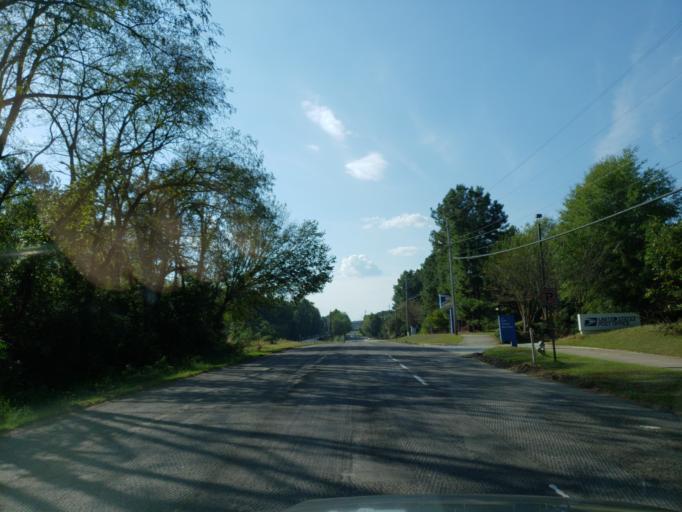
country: US
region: Georgia
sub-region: Cobb County
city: Powder Springs
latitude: 33.8628
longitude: -84.6900
